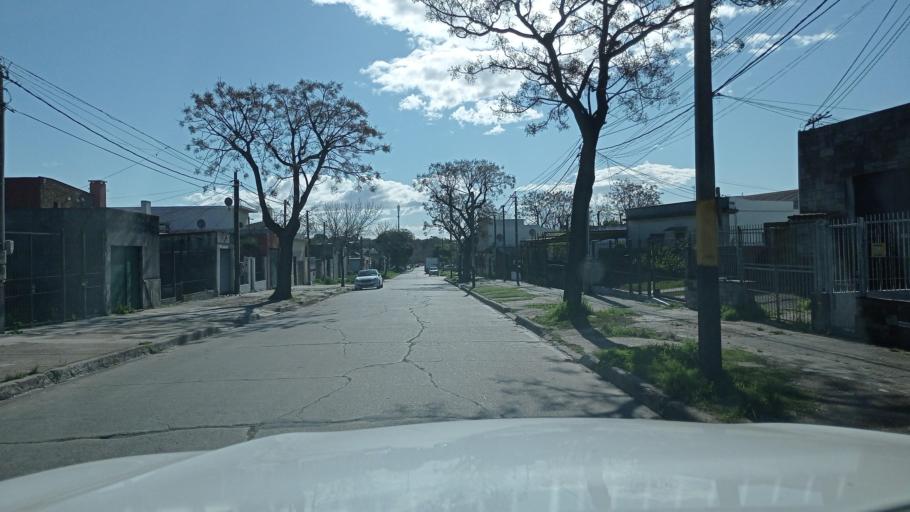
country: UY
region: Montevideo
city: Montevideo
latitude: -34.8532
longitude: -56.1545
